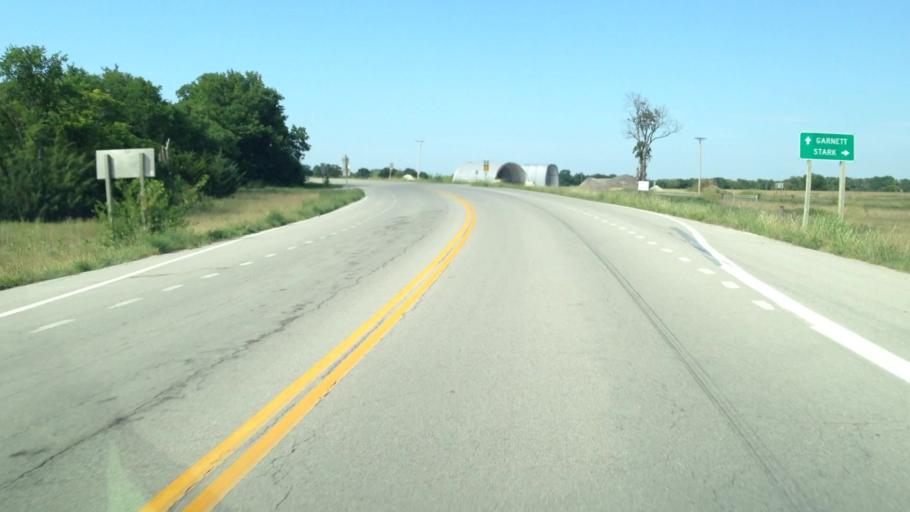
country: US
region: Kansas
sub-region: Neosho County
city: Erie
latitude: 37.6896
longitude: -95.1624
